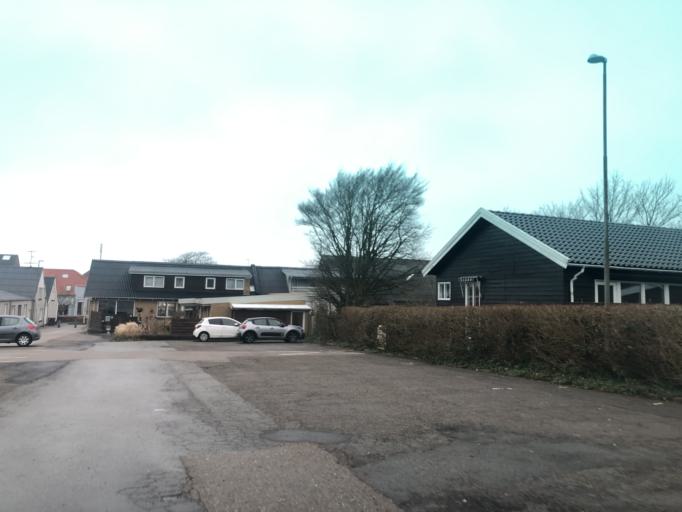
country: DK
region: North Denmark
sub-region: Thisted Kommune
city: Hurup
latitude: 56.7486
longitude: 8.4202
